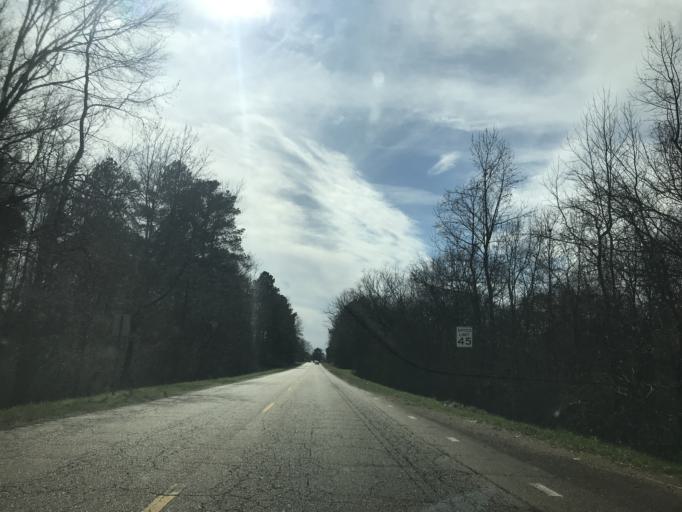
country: US
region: Mississippi
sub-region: Hinds County
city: Edwards
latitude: 32.1080
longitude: -90.6106
